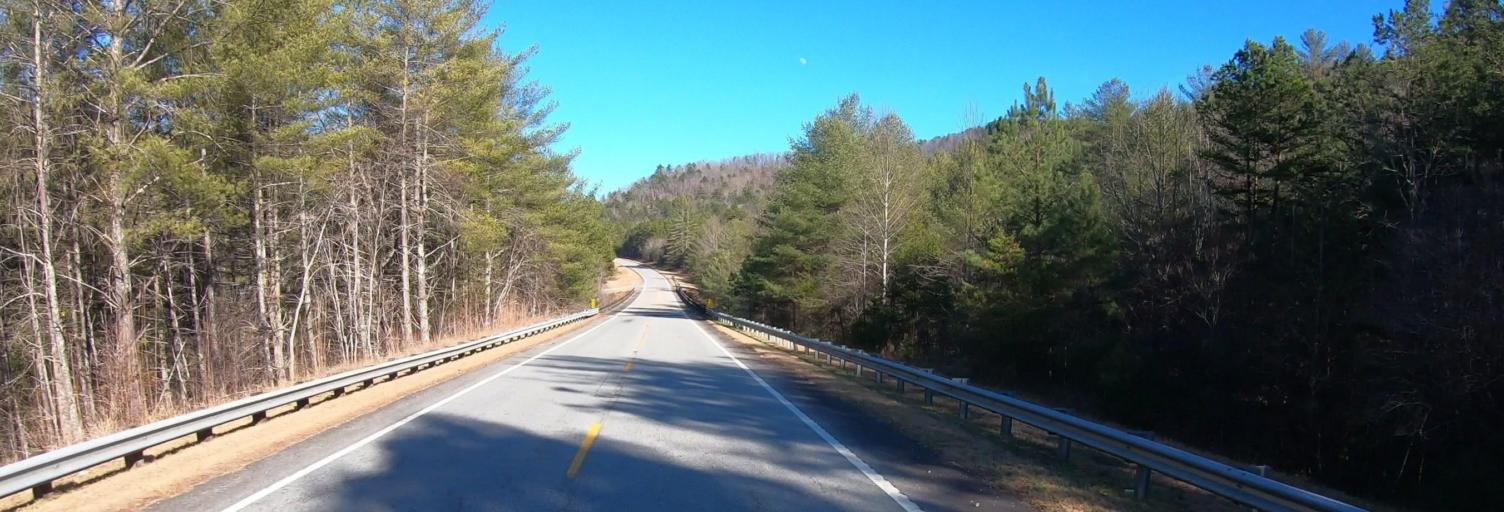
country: US
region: South Carolina
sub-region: Pickens County
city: Pickens
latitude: 34.9464
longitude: -82.8583
